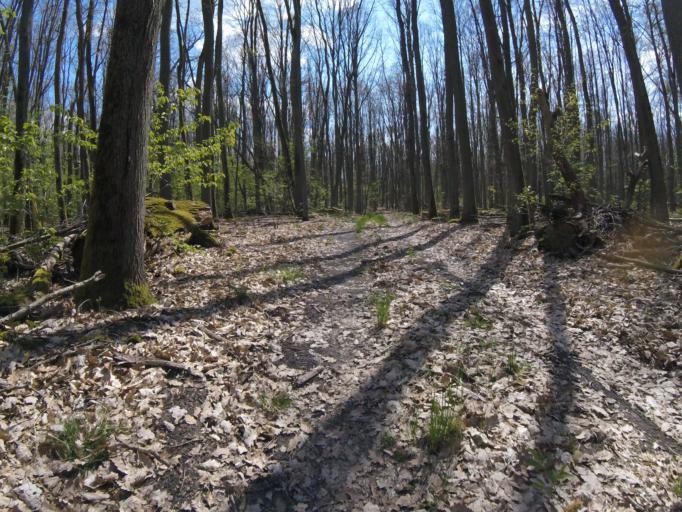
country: DE
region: Brandenburg
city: Gross Koris
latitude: 52.2038
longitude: 13.7221
